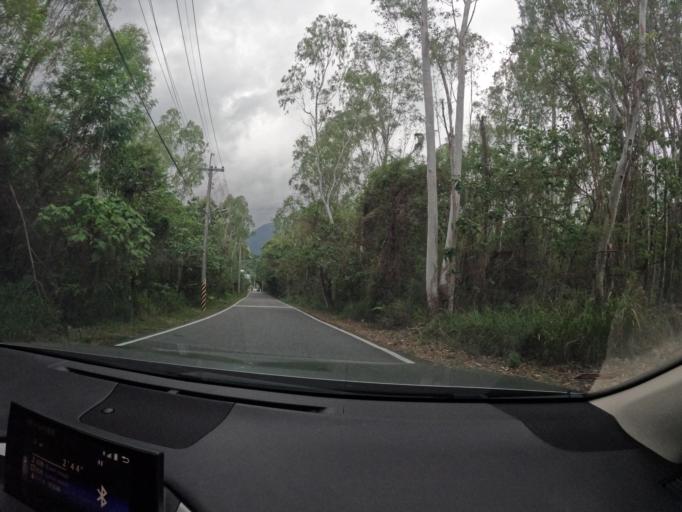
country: TW
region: Taiwan
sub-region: Hualien
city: Hualian
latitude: 24.0948
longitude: 121.6174
